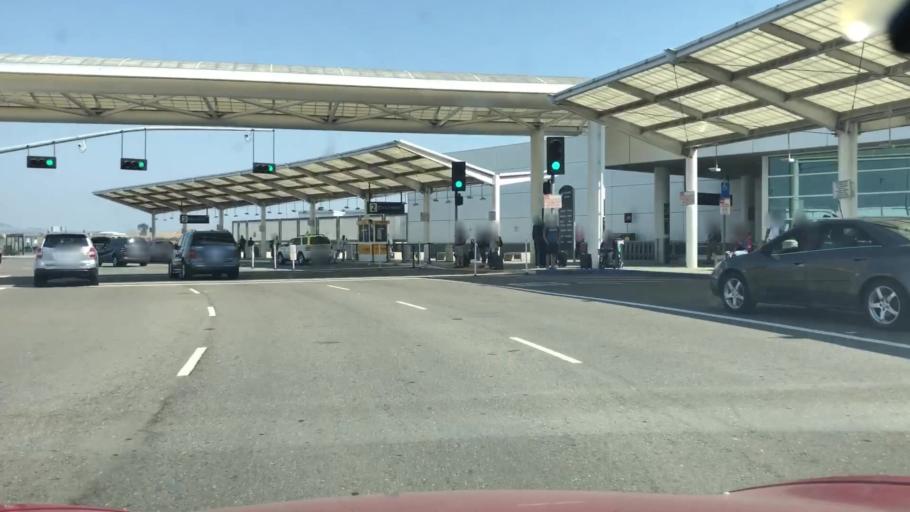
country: US
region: California
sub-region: Alameda County
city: San Leandro
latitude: 37.7116
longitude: -122.2114
